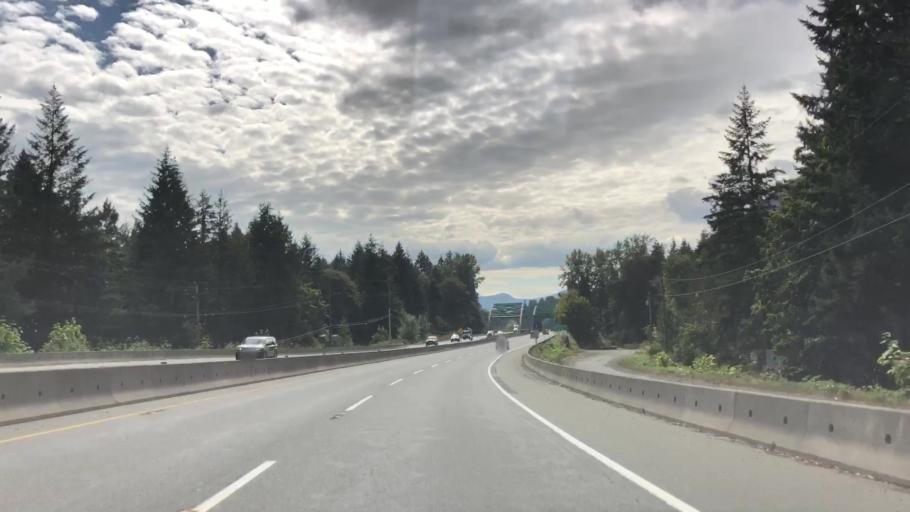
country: CA
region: British Columbia
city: North Cowichan
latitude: 48.8816
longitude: -123.7022
